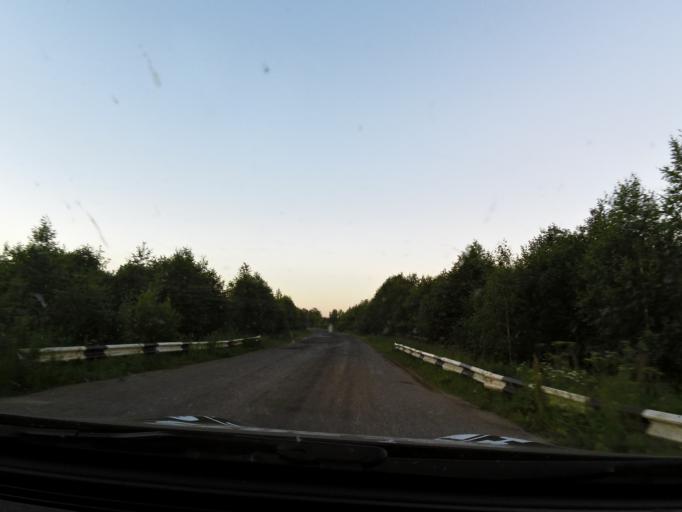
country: RU
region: Kostroma
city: Buy
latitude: 58.3564
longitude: 41.1958
